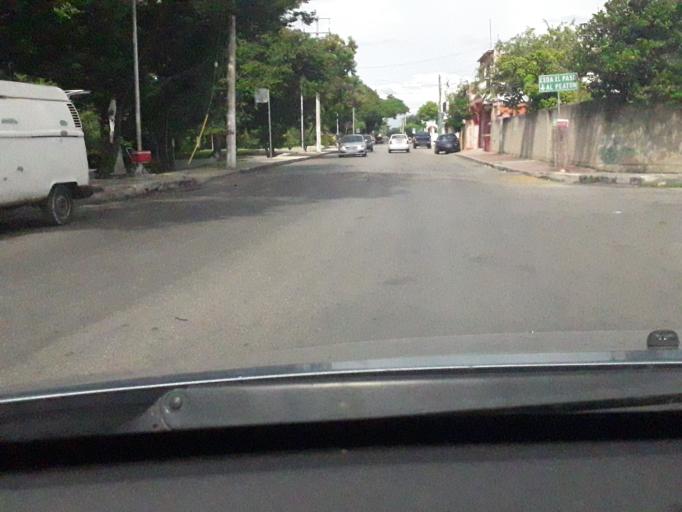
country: MX
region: Yucatan
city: Merida
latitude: 20.9742
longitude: -89.6558
